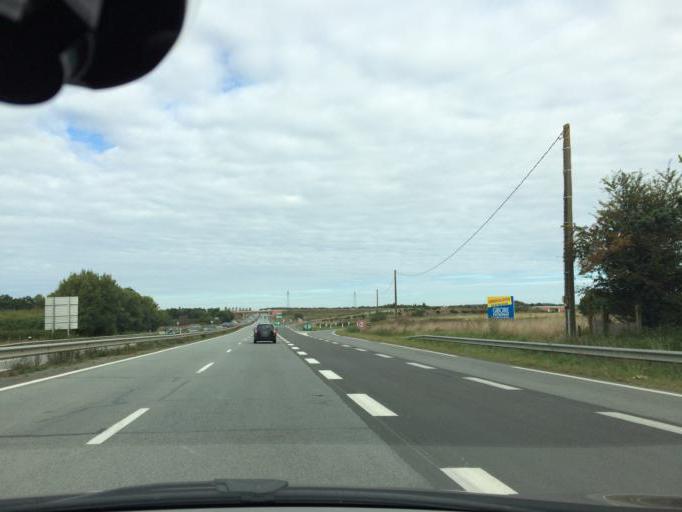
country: FR
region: Brittany
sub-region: Departement d'Ille-et-Vilaine
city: Miniac-Morvan
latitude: 48.5389
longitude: -1.9194
